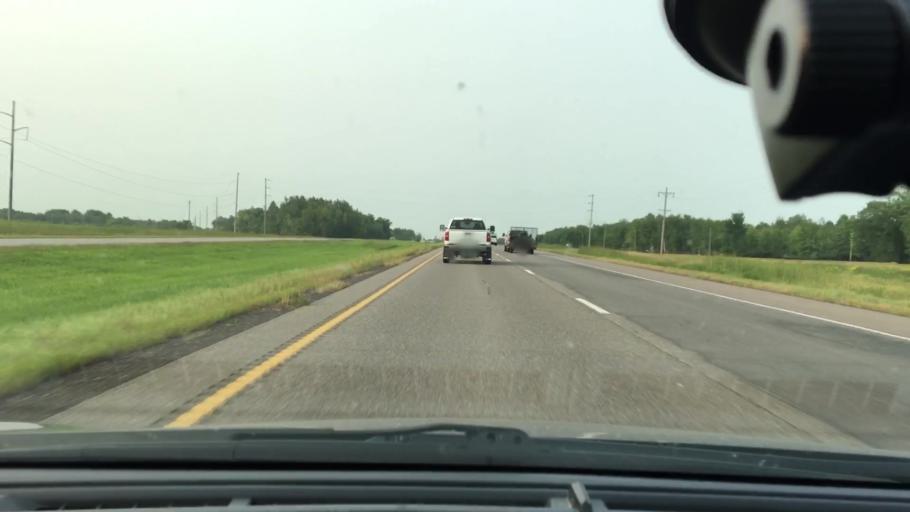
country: US
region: Minnesota
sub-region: Mille Lacs County
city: Milaca
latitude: 45.7407
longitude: -93.6373
